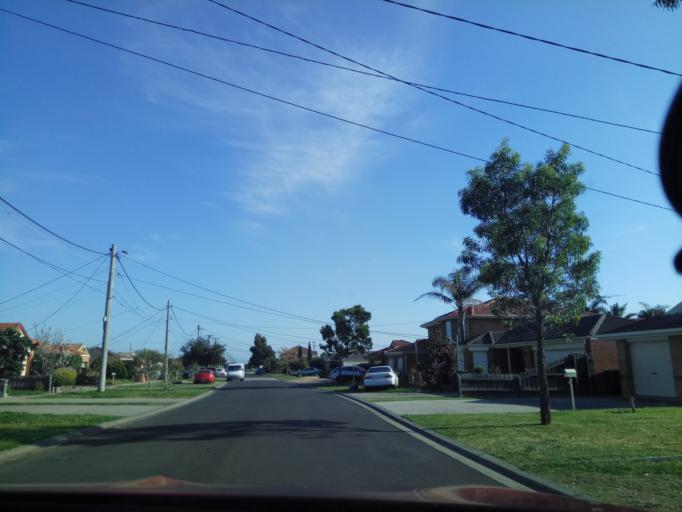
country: AU
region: Victoria
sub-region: Hobsons Bay
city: Laverton
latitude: -37.8716
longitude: 144.7695
